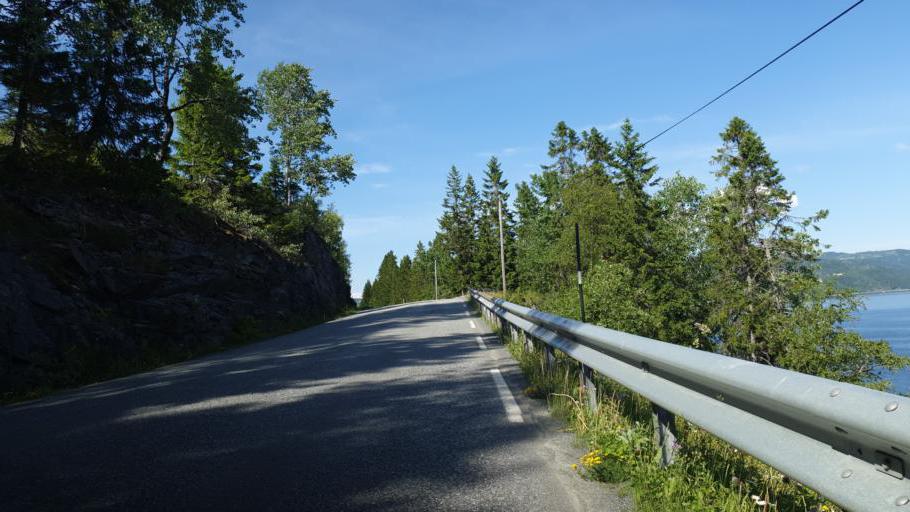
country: NO
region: Nord-Trondelag
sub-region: Leksvik
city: Leksvik
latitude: 63.6509
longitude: 10.6082
